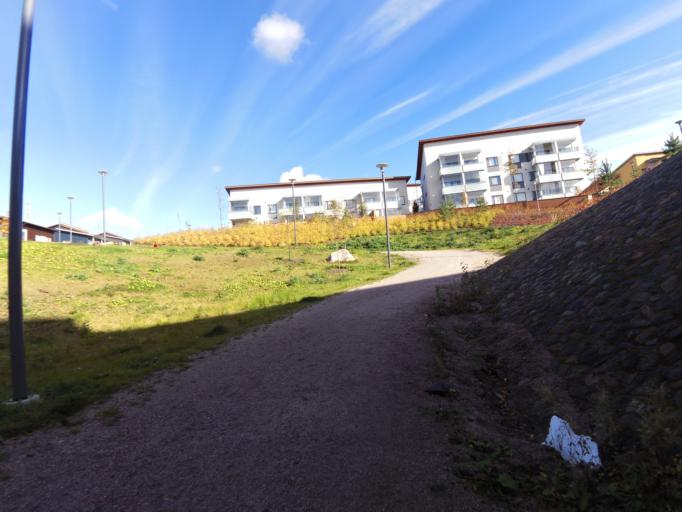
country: FI
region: Uusimaa
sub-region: Helsinki
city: Espoo
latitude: 60.1685
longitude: 24.6112
